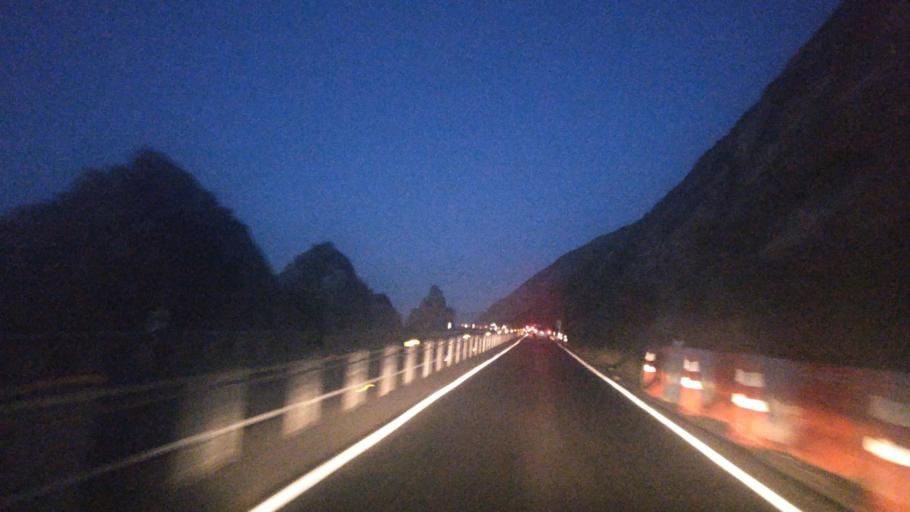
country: NZ
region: Wellington
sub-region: Porirua City
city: Porirua
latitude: -41.0211
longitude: 174.9102
